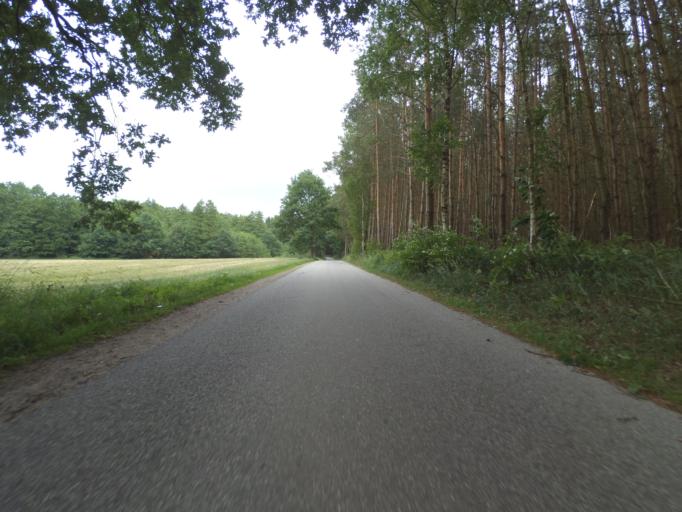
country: DE
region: Mecklenburg-Vorpommern
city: Lubz
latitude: 53.4149
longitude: 12.1369
